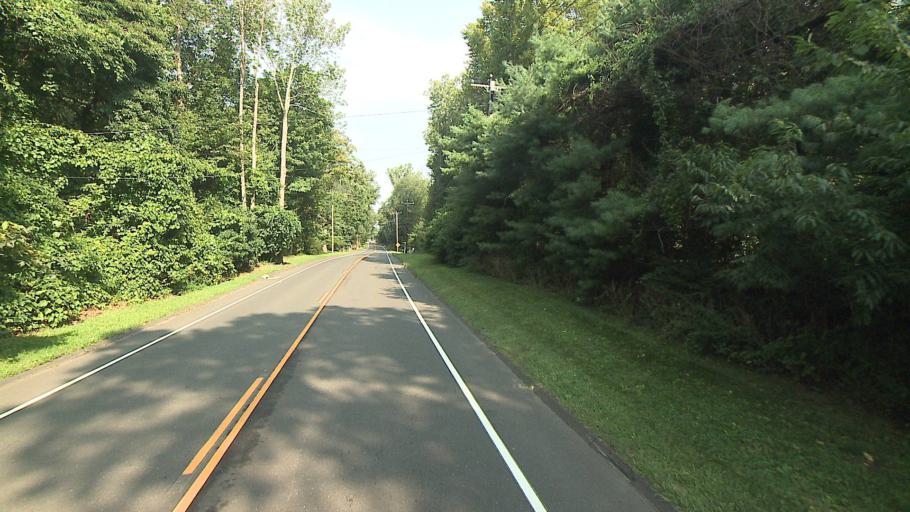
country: US
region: Connecticut
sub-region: Fairfield County
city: Westport
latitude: 41.1965
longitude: -73.3774
